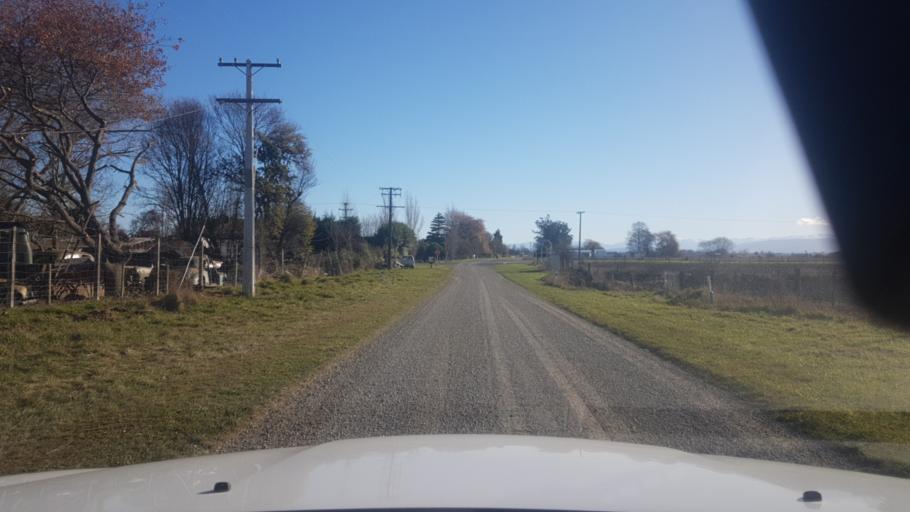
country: NZ
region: Canterbury
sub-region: Timaru District
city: Timaru
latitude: -44.2607
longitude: 171.3394
